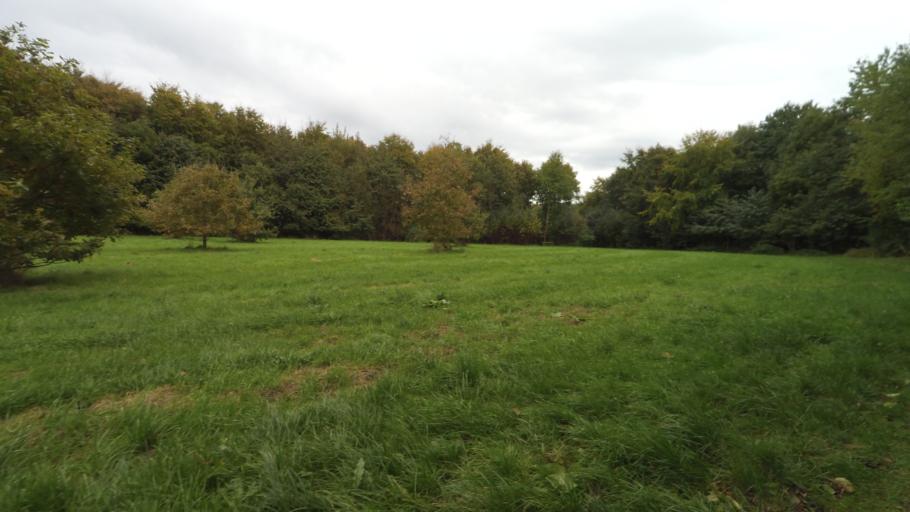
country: DK
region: Central Jutland
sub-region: Arhus Kommune
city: Stavtrup
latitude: 56.1356
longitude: 10.1271
